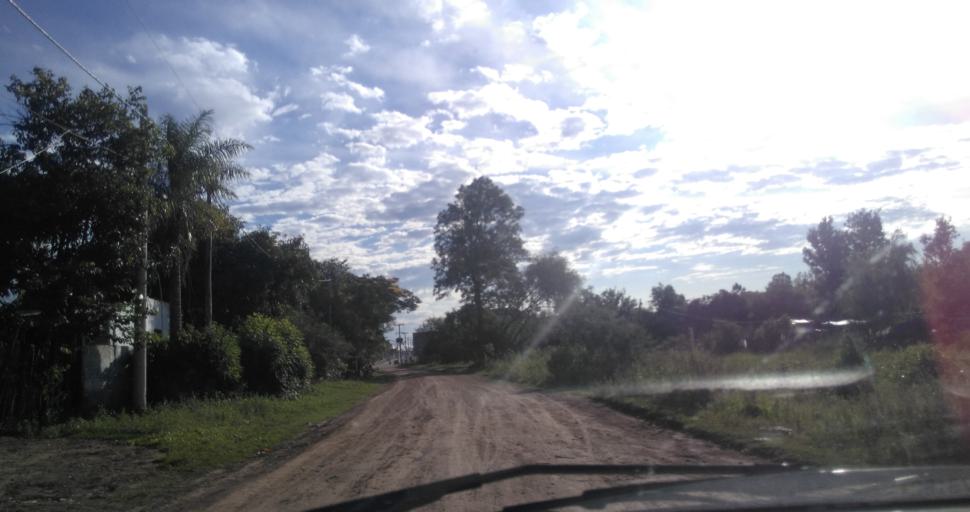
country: AR
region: Chaco
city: Fontana
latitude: -27.4107
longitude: -59.0293
